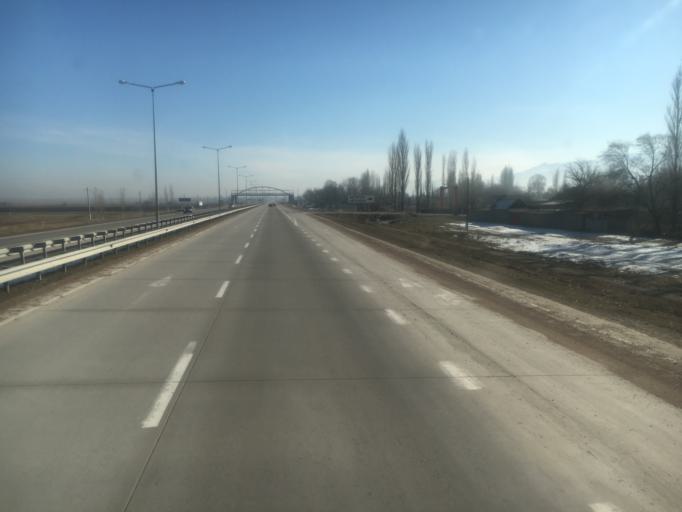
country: KZ
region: Zhambyl
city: Merke
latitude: 42.8768
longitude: 73.1084
